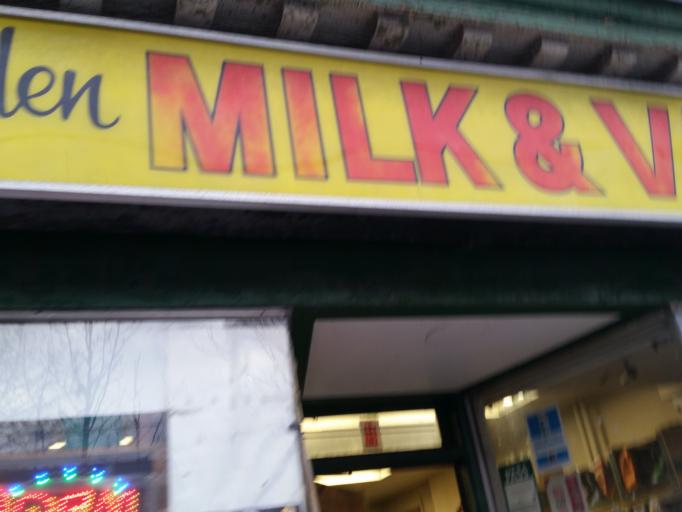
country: CA
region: Ontario
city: Toronto
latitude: 43.6483
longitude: -79.4496
